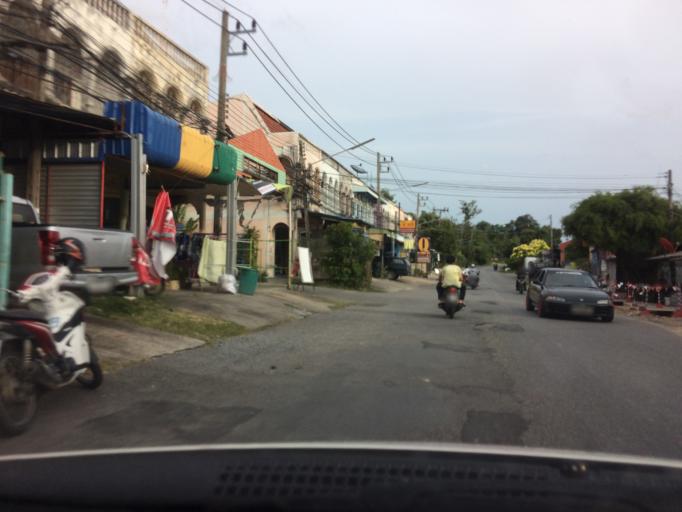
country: TH
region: Phuket
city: Phuket
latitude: 7.8951
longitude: 98.4071
